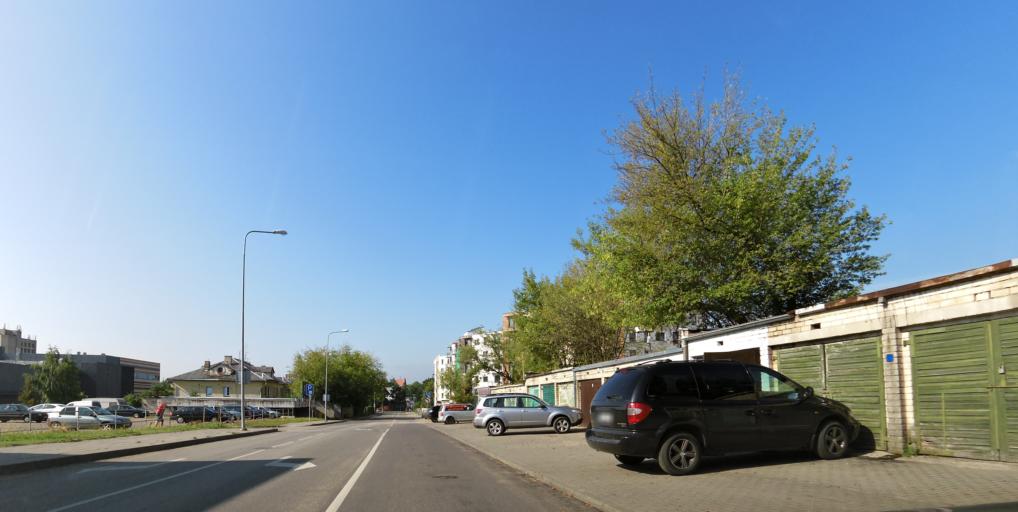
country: LT
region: Vilnius County
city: Seskine
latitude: 54.7018
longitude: 25.2564
